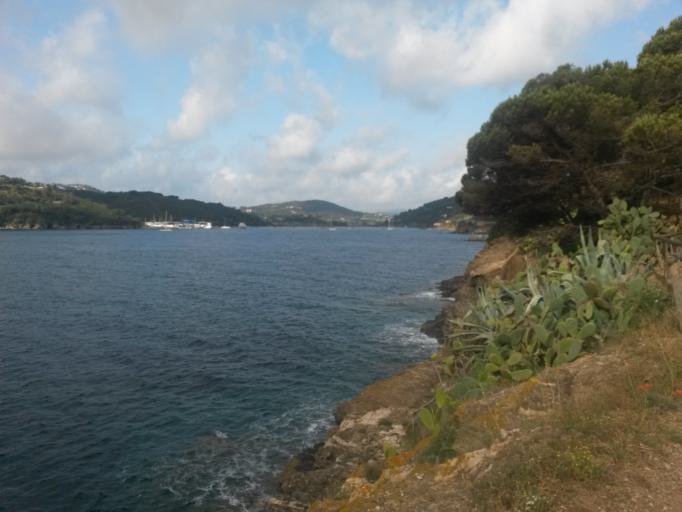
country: IT
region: Tuscany
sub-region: Provincia di Livorno
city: Porto Azzurro
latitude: 42.7631
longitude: 10.4025
